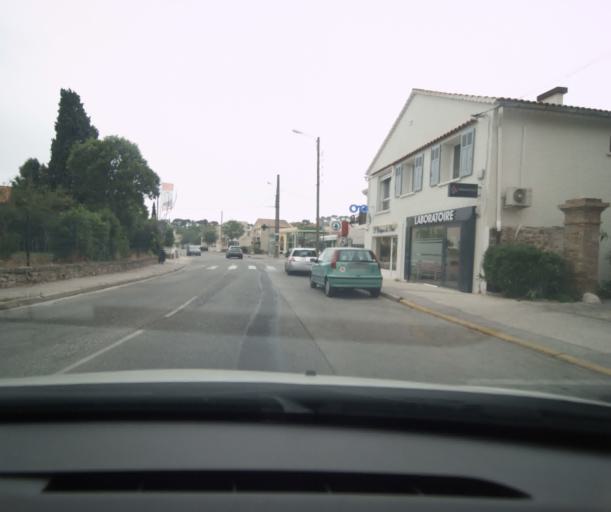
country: FR
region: Provence-Alpes-Cote d'Azur
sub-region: Departement du Var
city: La Valette-du-Var
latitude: 43.1171
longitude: 5.9809
